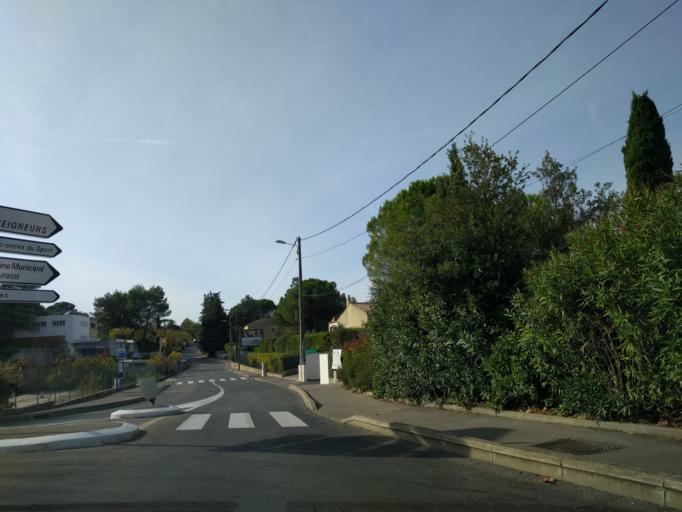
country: FR
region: Languedoc-Roussillon
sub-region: Departement de l'Herault
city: Montferrier-sur-Lez
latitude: 43.6435
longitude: 3.8604
